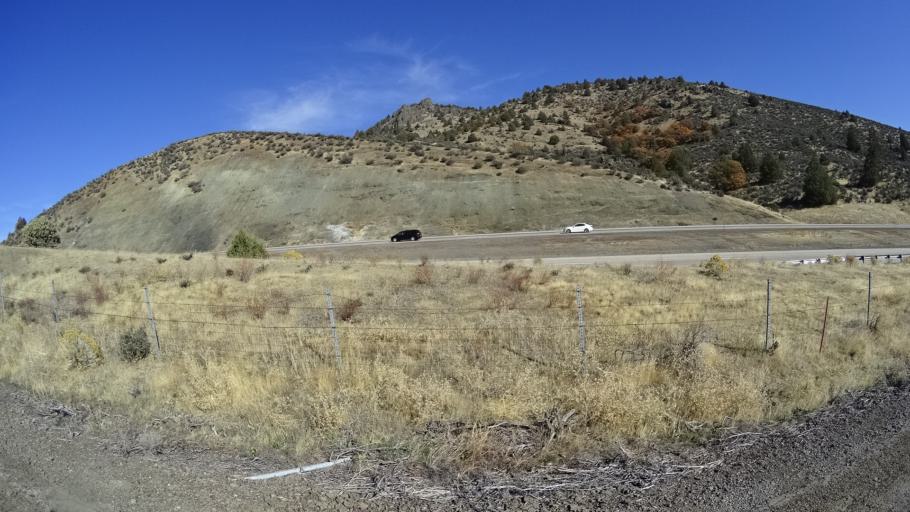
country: US
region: California
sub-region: Siskiyou County
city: Yreka
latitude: 41.7861
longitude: -122.5859
